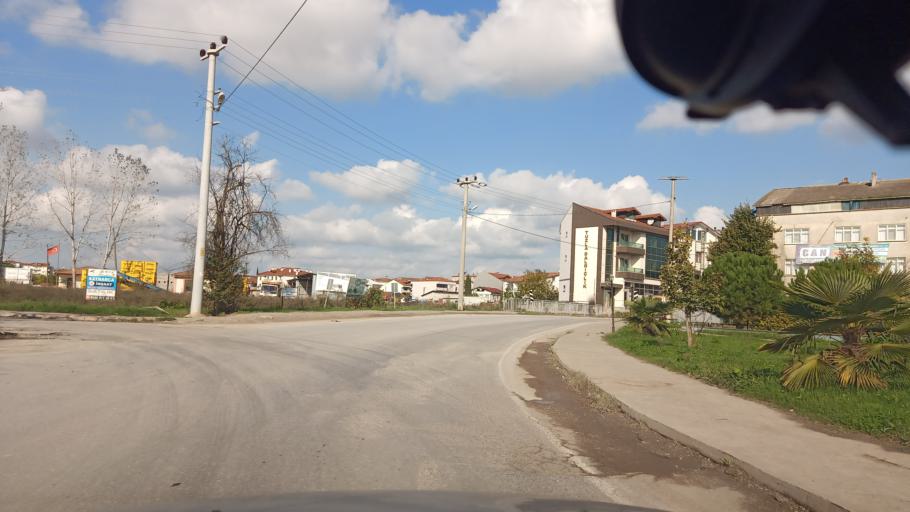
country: TR
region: Sakarya
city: Kaynarca
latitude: 41.0294
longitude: 30.3063
